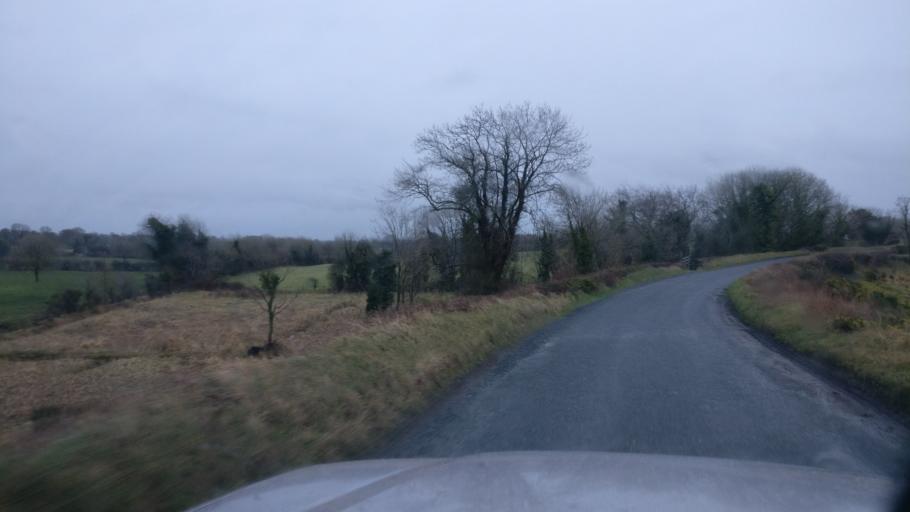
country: IE
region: Connaught
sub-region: County Galway
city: Ballinasloe
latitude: 53.3039
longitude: -8.2776
